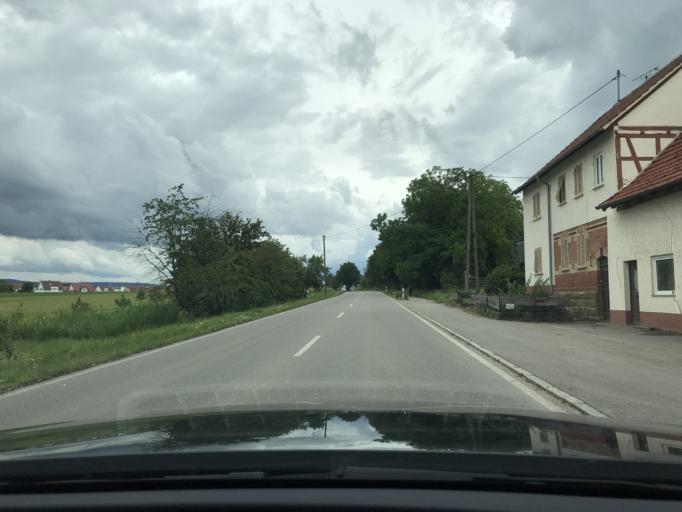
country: DE
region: Baden-Wuerttemberg
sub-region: Regierungsbezirk Stuttgart
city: Schwaikheim
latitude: 48.8843
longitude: 9.3550
